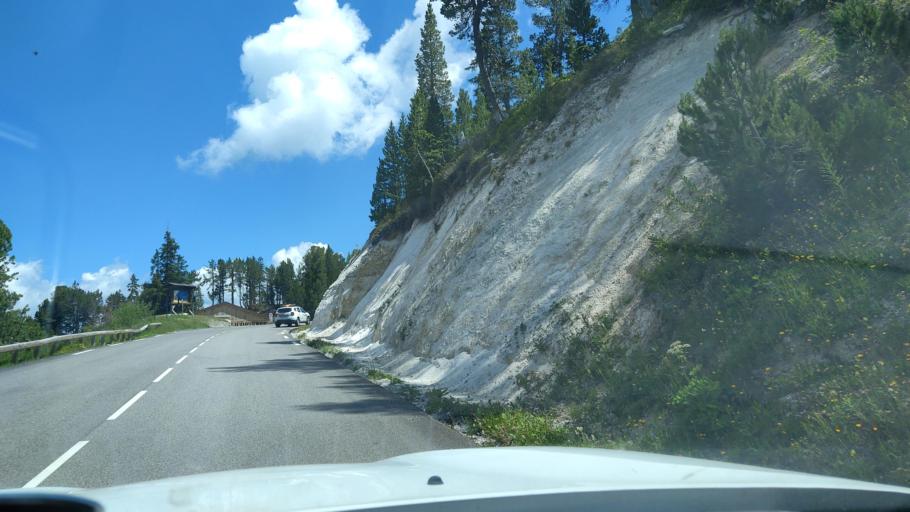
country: FR
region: Rhone-Alpes
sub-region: Departement de la Savoie
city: Seez
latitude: 45.5743
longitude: 6.8305
